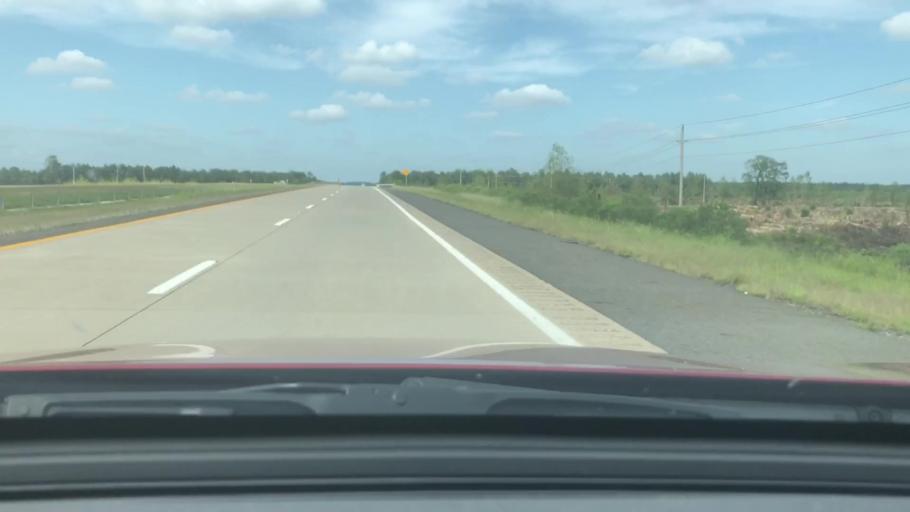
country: US
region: Texas
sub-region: Bowie County
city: Texarkana
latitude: 33.2222
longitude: -93.8733
